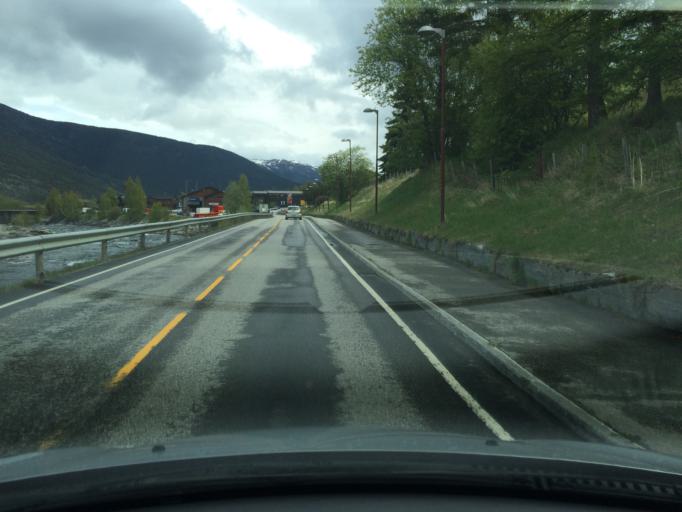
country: NO
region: Oppland
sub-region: Lom
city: Fossbergom
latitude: 61.8352
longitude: 8.5633
